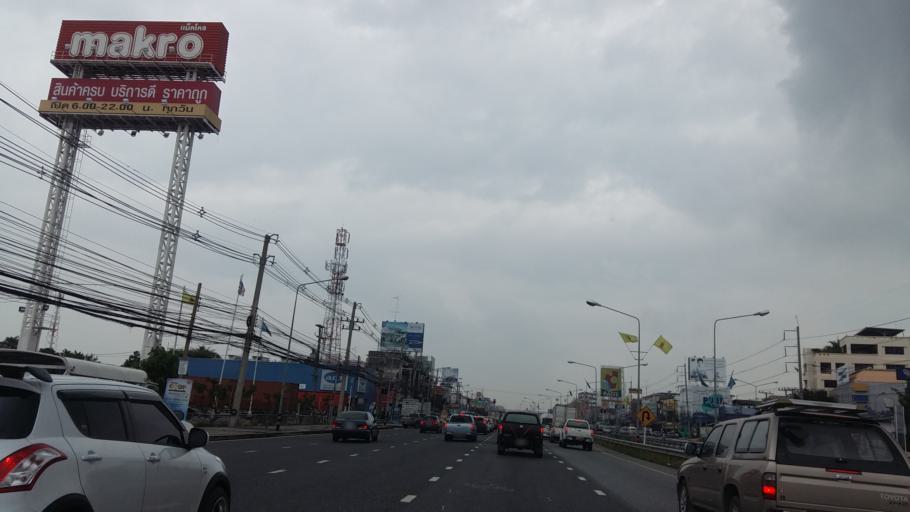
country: TH
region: Chon Buri
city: Chon Buri
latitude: 13.3211
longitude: 100.9614
